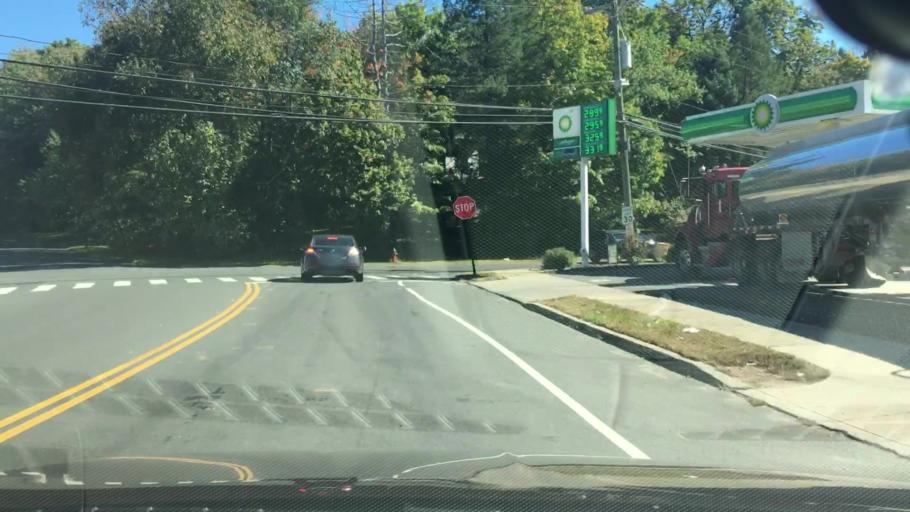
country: US
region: Connecticut
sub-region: Hartford County
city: Plainville
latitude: 41.6797
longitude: -72.9039
